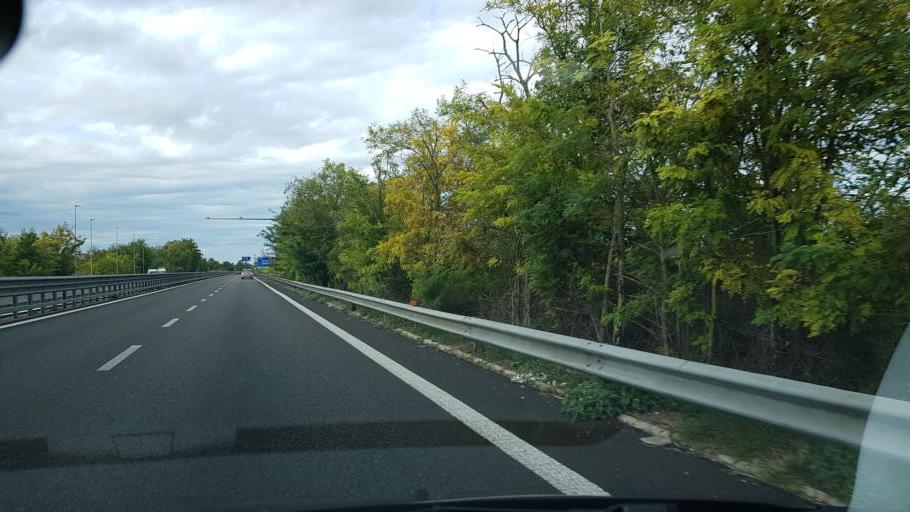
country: IT
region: Apulia
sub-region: Provincia di Lecce
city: Castromediano
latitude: 40.3196
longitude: 18.1874
